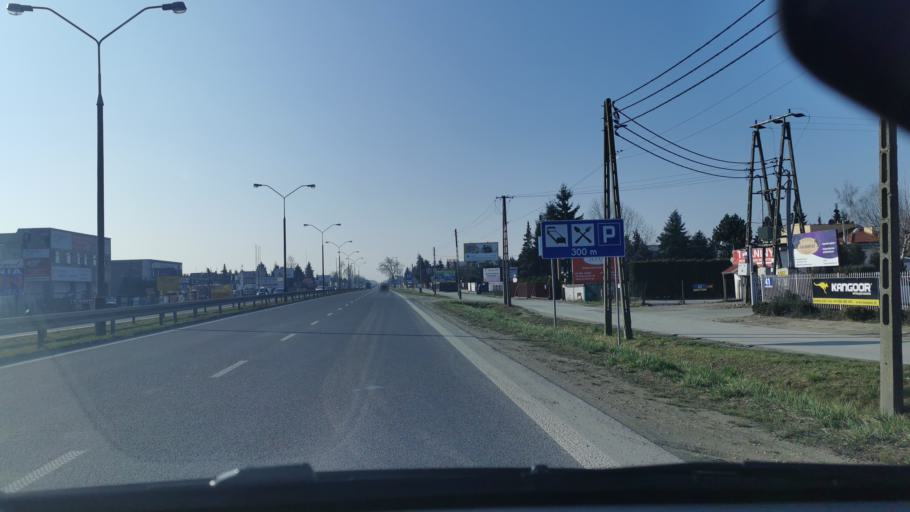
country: PL
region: Masovian Voivodeship
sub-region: Powiat pruszkowski
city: Nowe Grocholice
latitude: 52.1276
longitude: 20.8960
